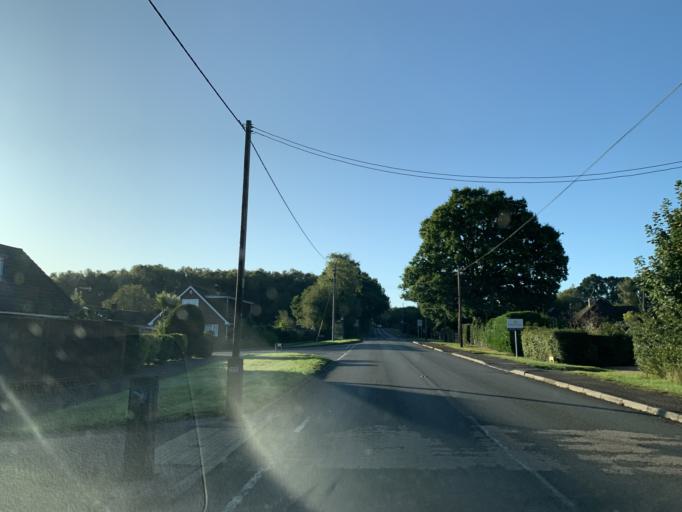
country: GB
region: England
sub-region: Wiltshire
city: Whiteparish
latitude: 50.9683
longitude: -1.6352
